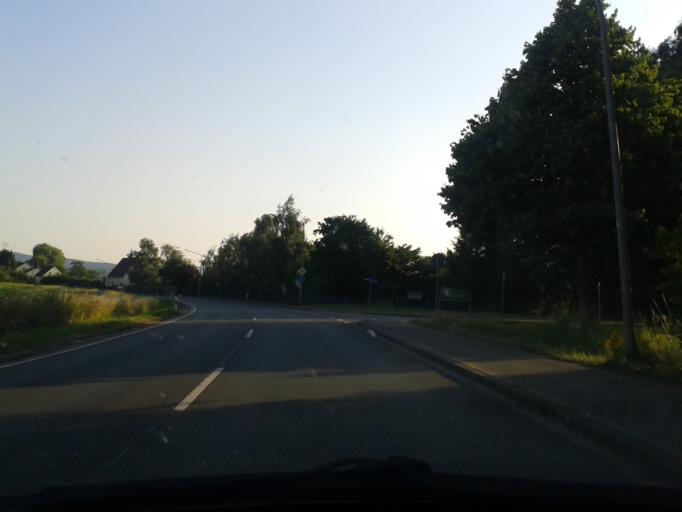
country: DE
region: North Rhine-Westphalia
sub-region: Regierungsbezirk Detmold
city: Detmold
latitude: 51.9289
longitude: 8.9197
